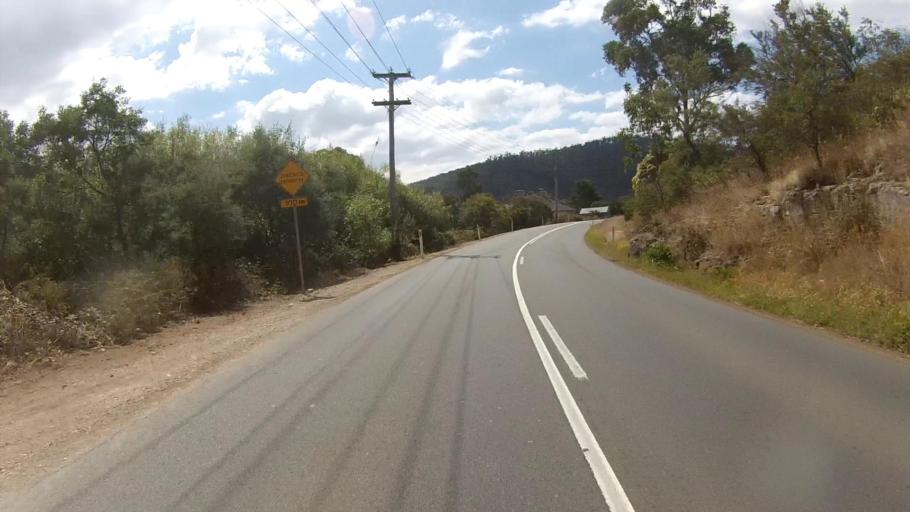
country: AU
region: Tasmania
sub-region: Clarence
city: Cambridge
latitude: -42.8418
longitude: 147.4212
